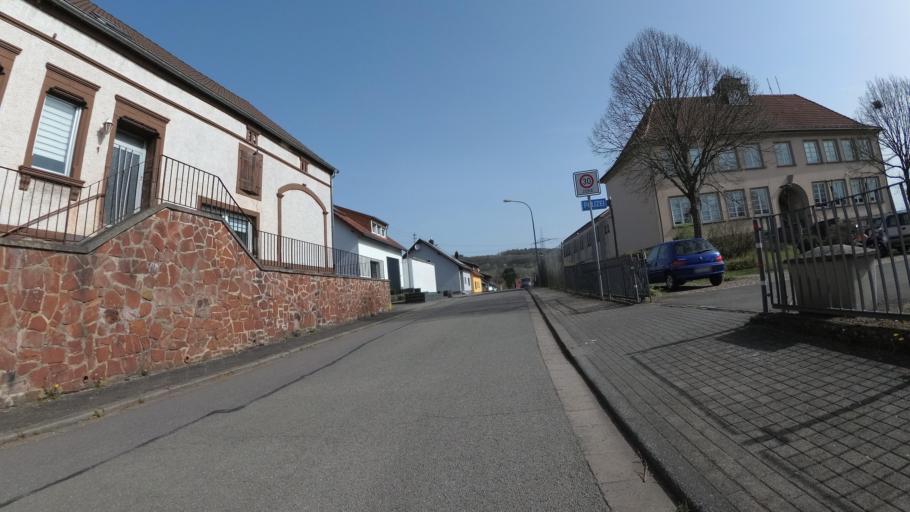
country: DE
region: Saarland
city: Illingen
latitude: 49.3848
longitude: 7.0443
